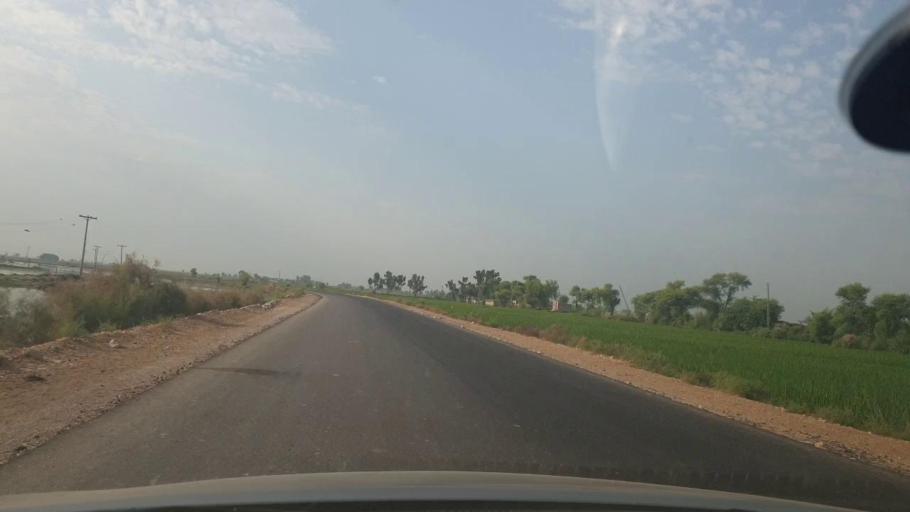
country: PK
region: Sindh
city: Jacobabad
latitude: 28.1043
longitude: 68.3259
